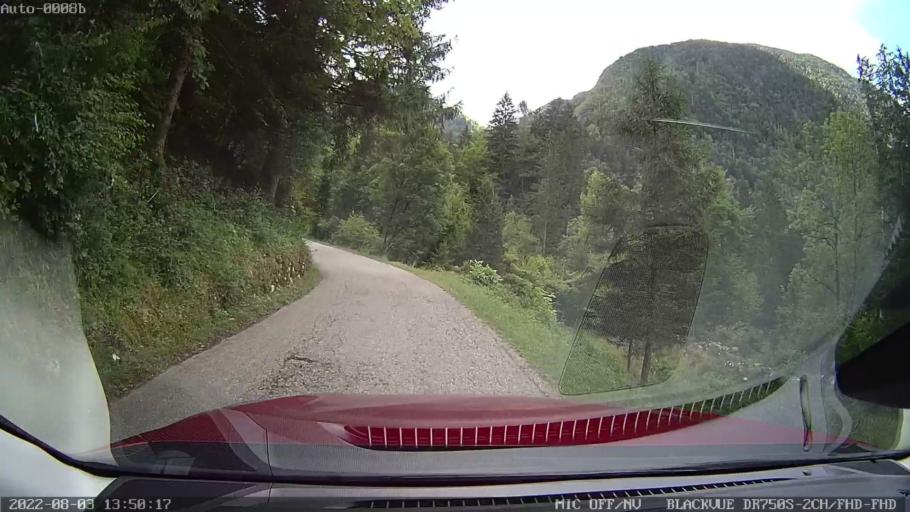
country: SI
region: Bovec
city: Bovec
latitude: 46.3388
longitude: 13.6849
